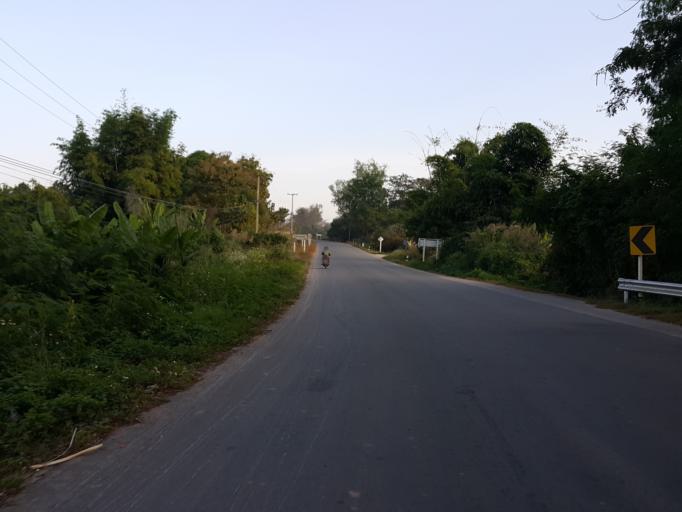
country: TH
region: Lamphun
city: Thung Hua Chang
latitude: 17.9819
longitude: 99.0354
